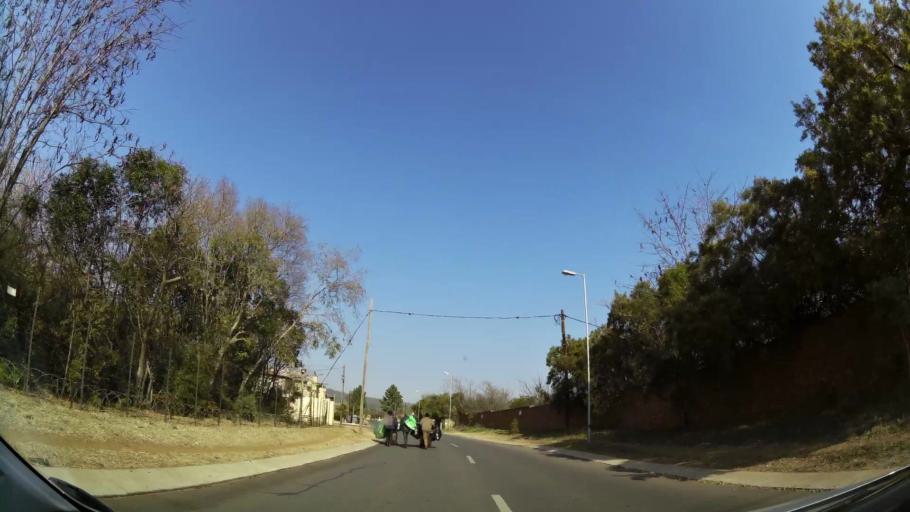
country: ZA
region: Gauteng
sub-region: City of Tshwane Metropolitan Municipality
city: Pretoria
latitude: -25.7575
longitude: 28.3289
